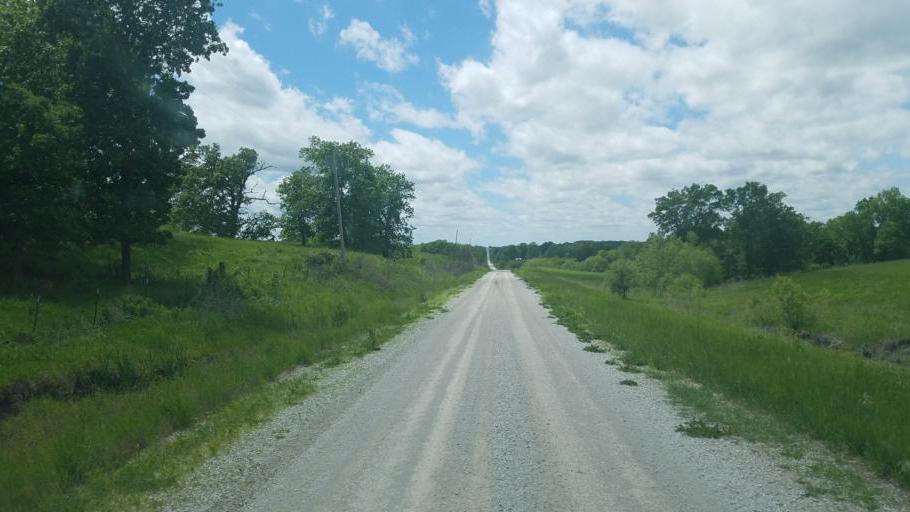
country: US
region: Iowa
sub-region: Decatur County
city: Lamoni
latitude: 40.5005
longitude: -93.9970
